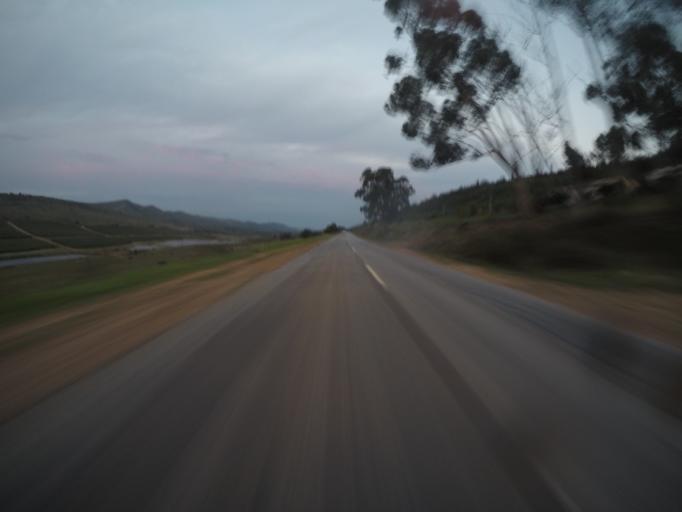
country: ZA
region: Western Cape
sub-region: Eden District Municipality
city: Plettenberg Bay
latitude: -33.8051
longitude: 23.6751
